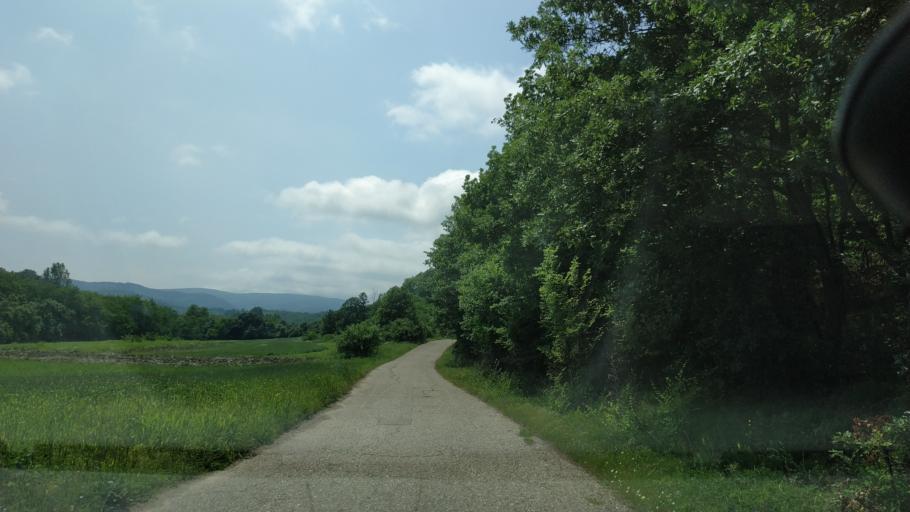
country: RS
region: Central Serbia
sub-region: Nisavski Okrug
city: Aleksinac
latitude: 43.4288
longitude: 21.7316
